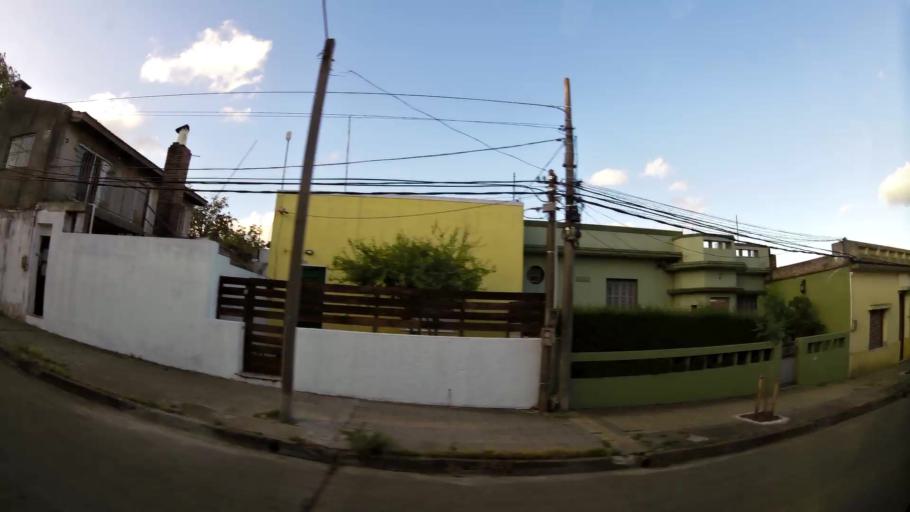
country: UY
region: Montevideo
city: Montevideo
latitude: -34.8833
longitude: -56.2504
